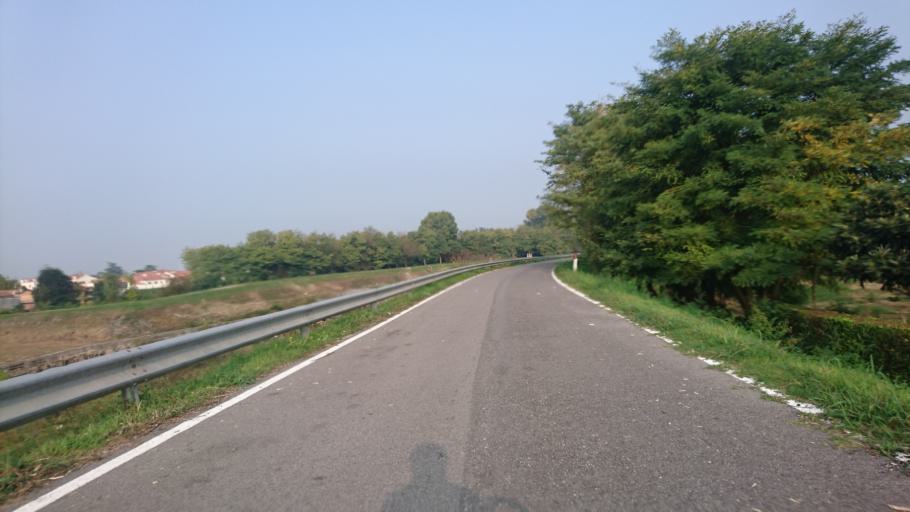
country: IT
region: Veneto
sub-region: Provincia di Padova
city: Limena
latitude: 45.4809
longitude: 11.8478
